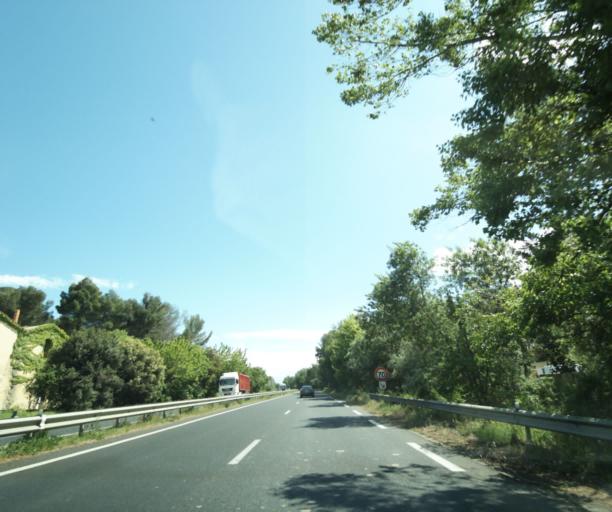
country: FR
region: Languedoc-Roussillon
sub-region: Departement de l'Herault
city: Juvignac
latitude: 43.6041
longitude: 3.8197
